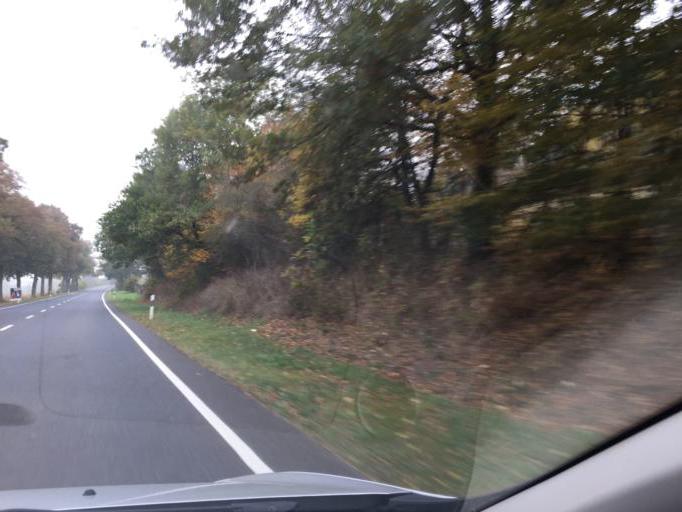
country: LU
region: Grevenmacher
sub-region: Canton de Remich
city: Waldbredimus
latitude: 49.5643
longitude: 6.2958
